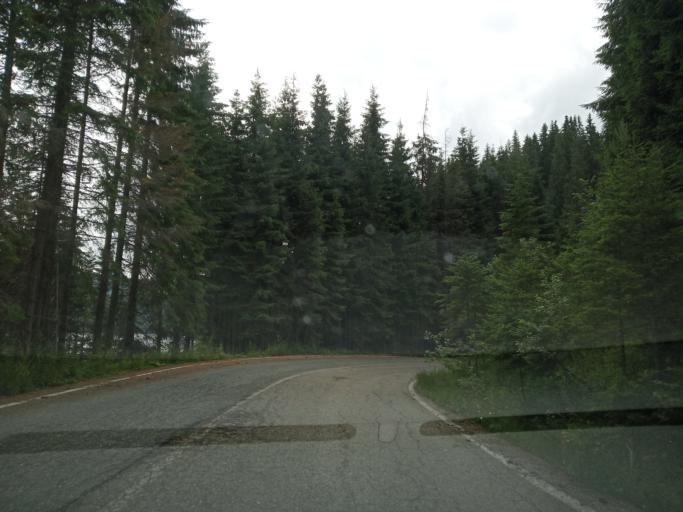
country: RO
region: Valcea
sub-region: Comuna Voineasa
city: Voineasa
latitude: 45.4229
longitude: 23.7390
